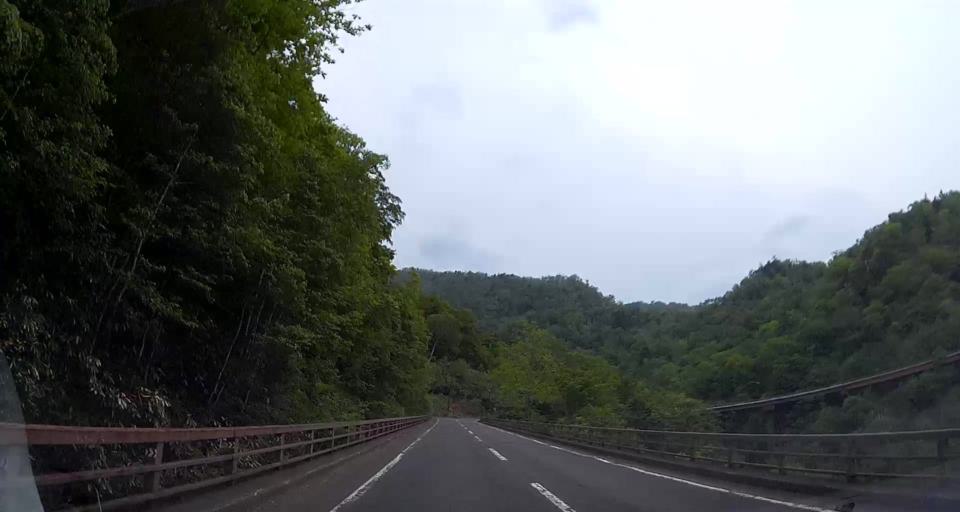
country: JP
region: Hokkaido
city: Shiraoi
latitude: 42.6546
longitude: 141.1851
